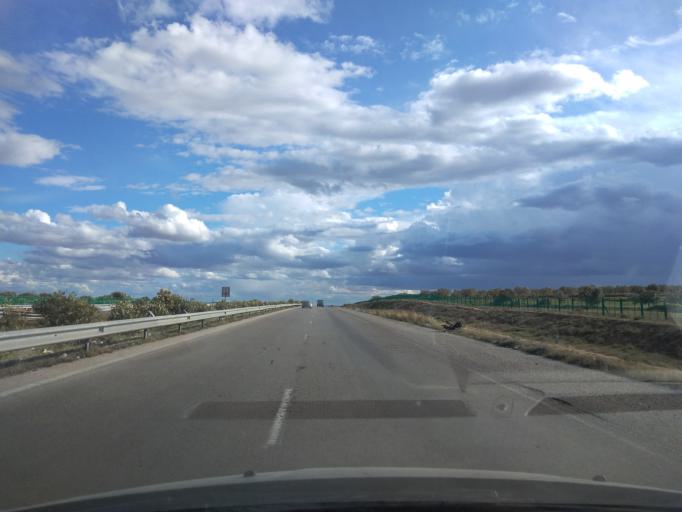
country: TN
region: Al Munastir
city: Manzil Kamil
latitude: 35.5488
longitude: 10.6201
